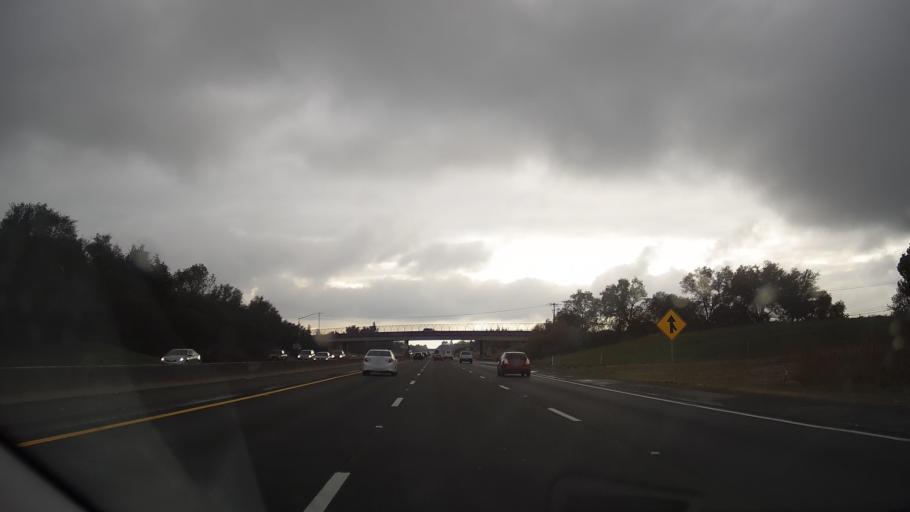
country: US
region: California
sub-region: Placer County
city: Loomis
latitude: 38.8353
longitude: -121.1671
